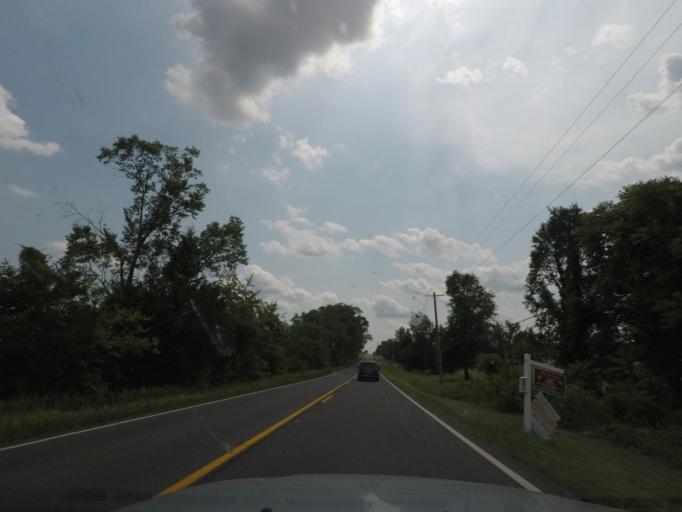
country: US
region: Virginia
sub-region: Culpeper County
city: Merrimac
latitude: 38.4328
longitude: -78.0302
